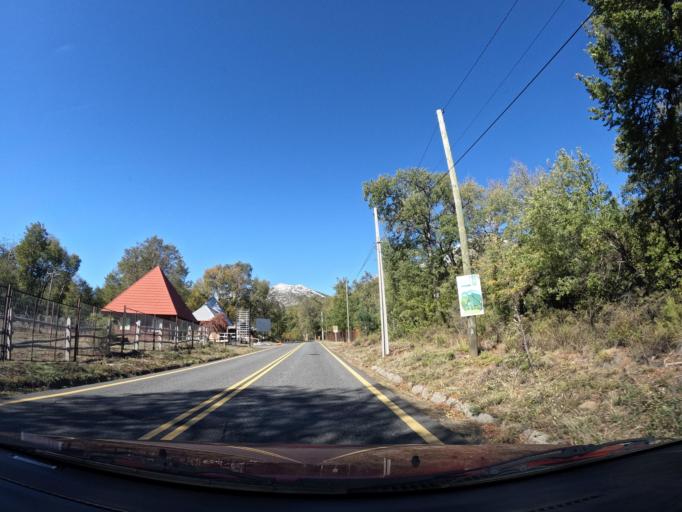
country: CL
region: Biobio
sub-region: Provincia de Nuble
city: Coihueco
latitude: -36.9067
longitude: -71.5281
